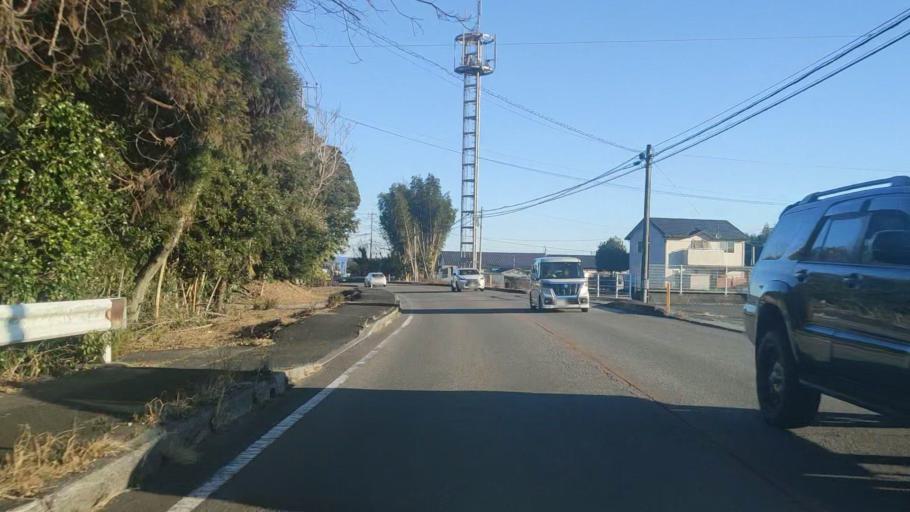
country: JP
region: Miyazaki
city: Takanabe
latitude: 32.1780
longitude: 131.5216
